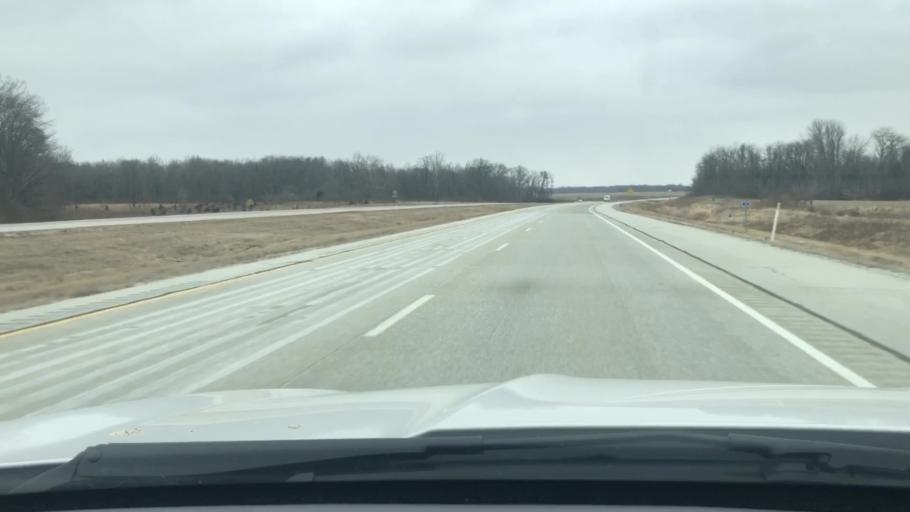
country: US
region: Indiana
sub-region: Tippecanoe County
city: Battle Ground
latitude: 40.4864
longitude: -86.7720
